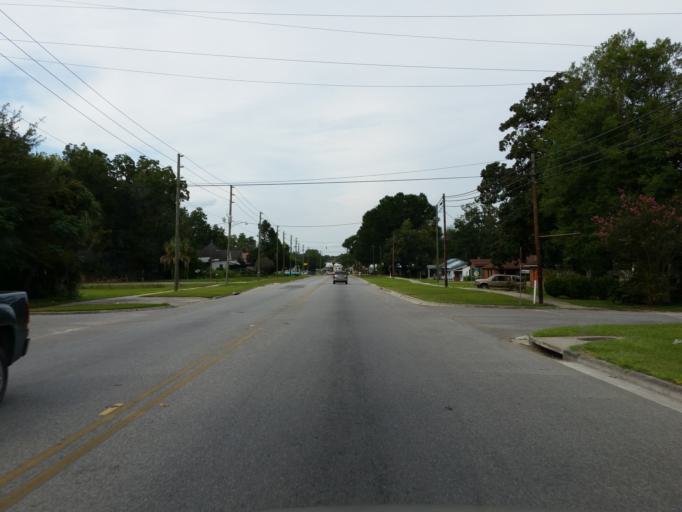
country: US
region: Florida
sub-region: Suwannee County
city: Live Oak
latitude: 30.3014
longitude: -82.9867
